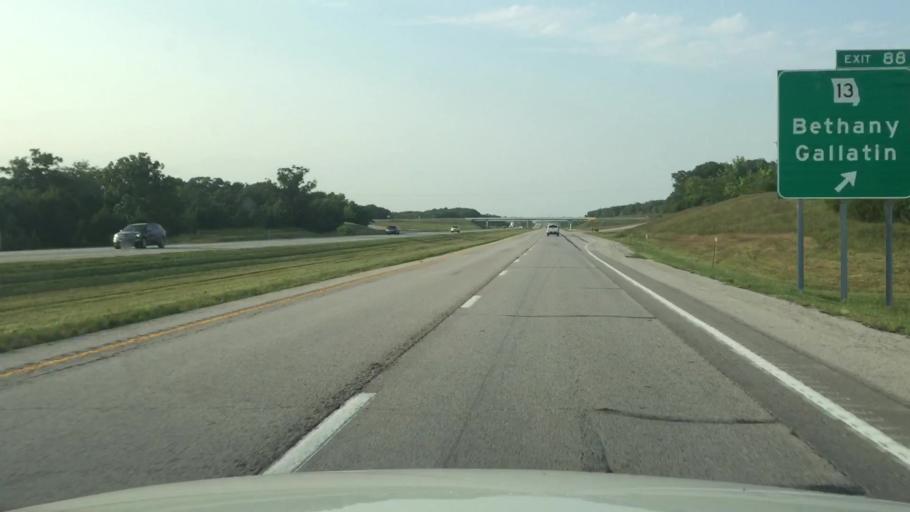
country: US
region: Missouri
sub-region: Harrison County
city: Bethany
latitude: 40.2048
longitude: -94.0136
